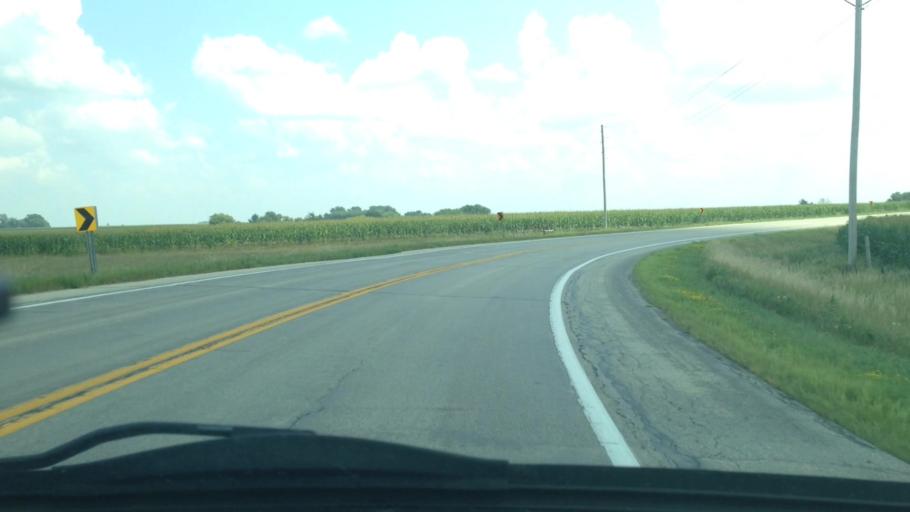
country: US
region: Minnesota
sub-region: Olmsted County
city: Rochester
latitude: 43.9456
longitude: -92.4100
